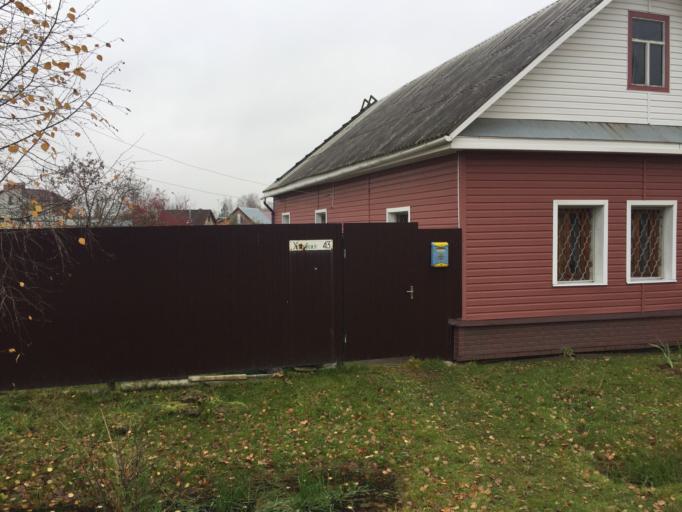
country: RU
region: Jaroslavl
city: Yaroslavl
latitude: 57.7220
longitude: 39.7701
